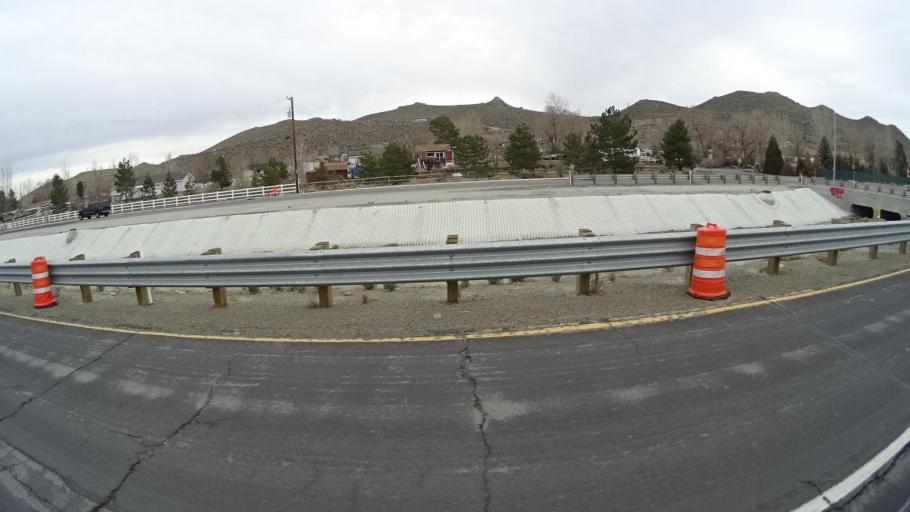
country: US
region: Nevada
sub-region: Washoe County
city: Lemmon Valley
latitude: 39.6292
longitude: -119.8465
